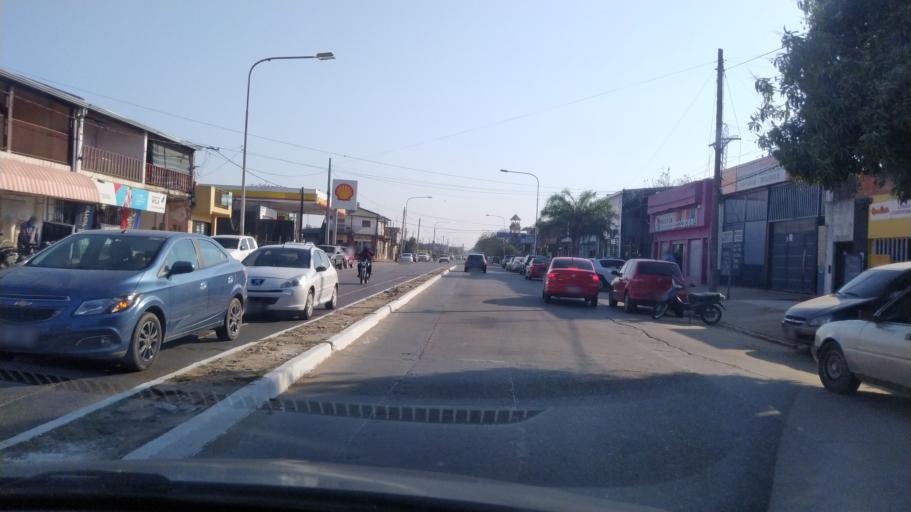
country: AR
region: Corrientes
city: Corrientes
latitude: -27.4864
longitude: -58.8161
